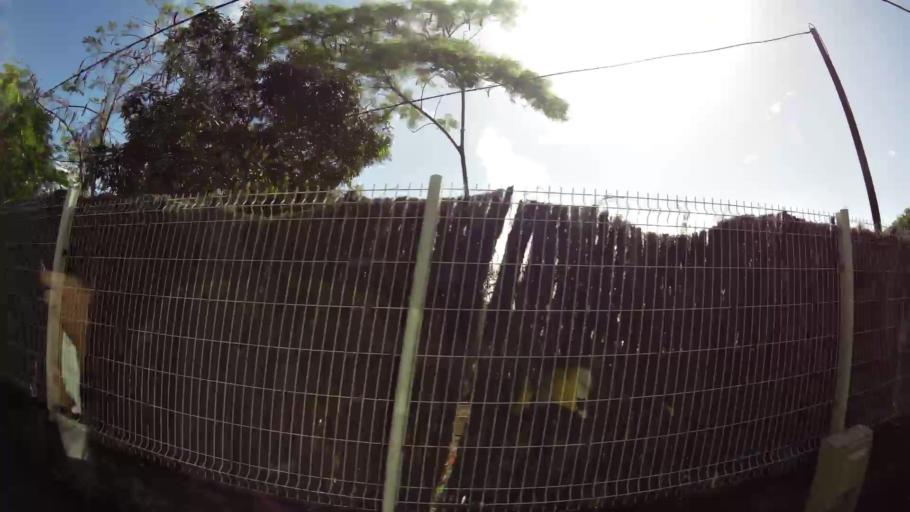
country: MQ
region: Martinique
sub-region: Martinique
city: Les Trois-Ilets
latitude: 14.4633
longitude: -61.0476
